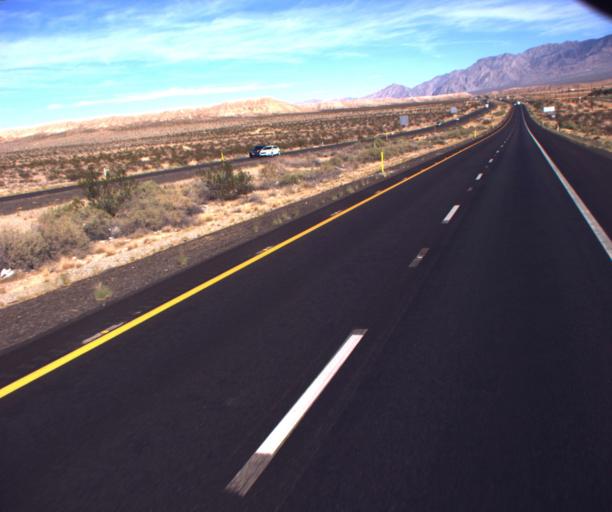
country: US
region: Nevada
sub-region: Clark County
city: Mesquite
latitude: 36.8190
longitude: -114.0446
